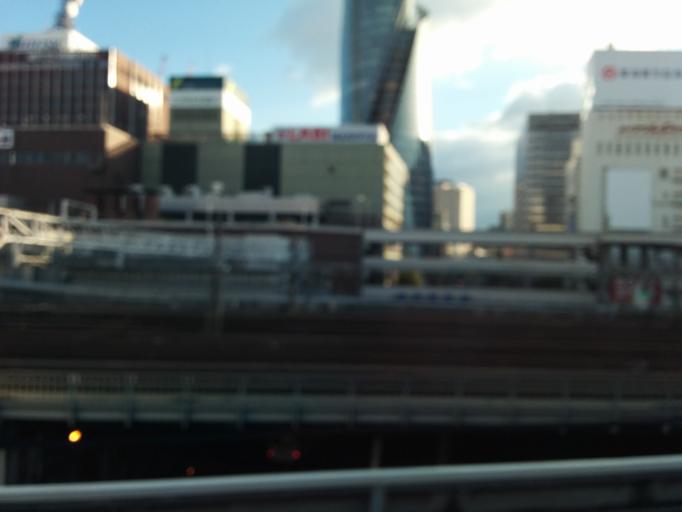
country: JP
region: Aichi
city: Nagoya-shi
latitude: 35.1675
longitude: 136.8829
